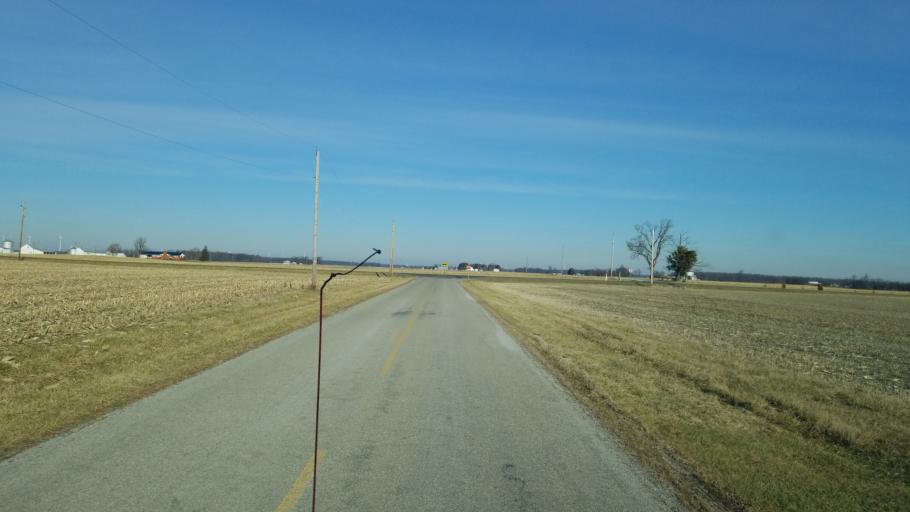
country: US
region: Ohio
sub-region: Hardin County
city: Kenton
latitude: 40.7311
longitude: -83.6914
